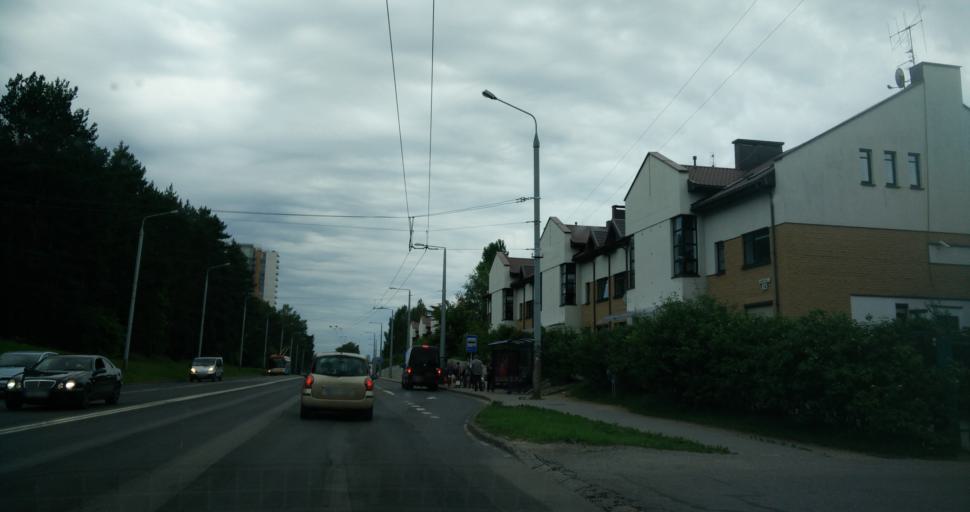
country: LT
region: Vilnius County
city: Rasos
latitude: 54.7264
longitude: 25.3253
